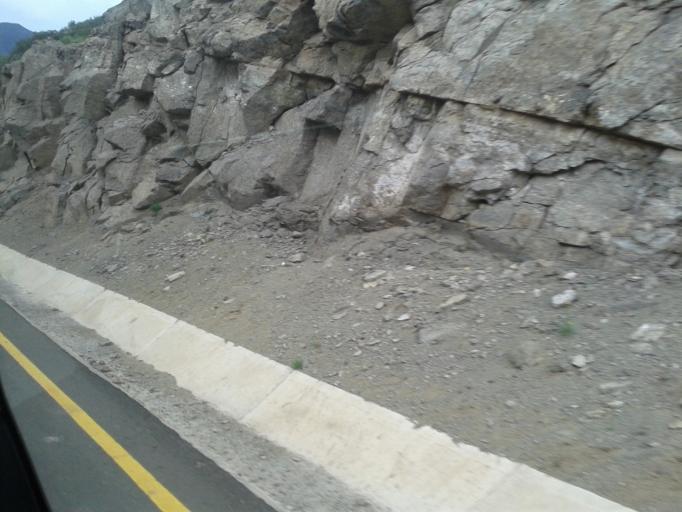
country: LS
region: Maseru
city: Nako
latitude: -29.6558
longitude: 27.8480
